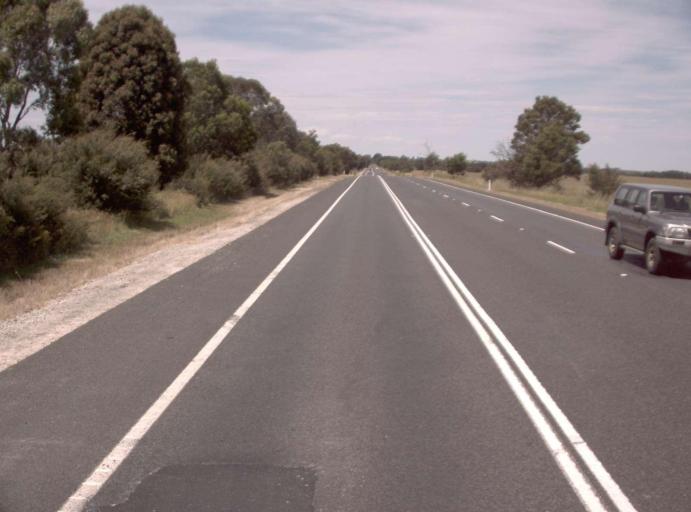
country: AU
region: Victoria
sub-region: Wellington
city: Heyfield
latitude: -38.1177
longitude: 146.8652
